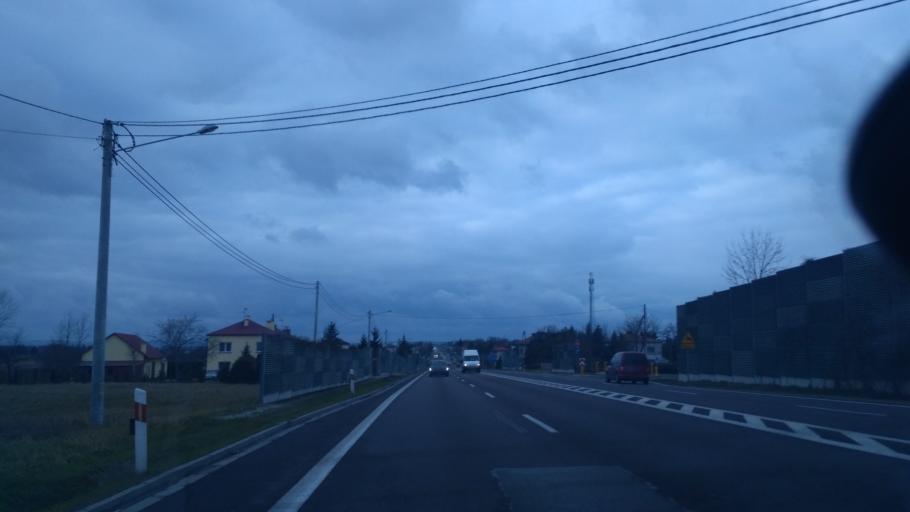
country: PL
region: Subcarpathian Voivodeship
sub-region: Powiat rzeszowski
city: Krasne
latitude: 50.0421
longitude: 22.1064
